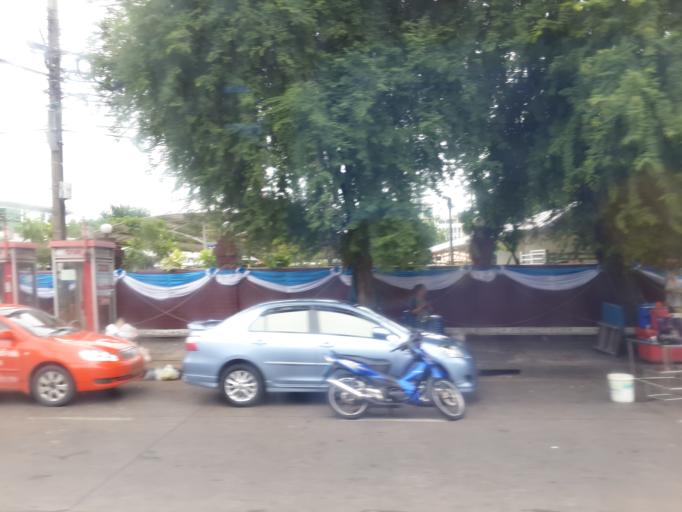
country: TH
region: Bangkok
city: Phra Nakhon
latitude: 13.7698
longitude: 100.5057
